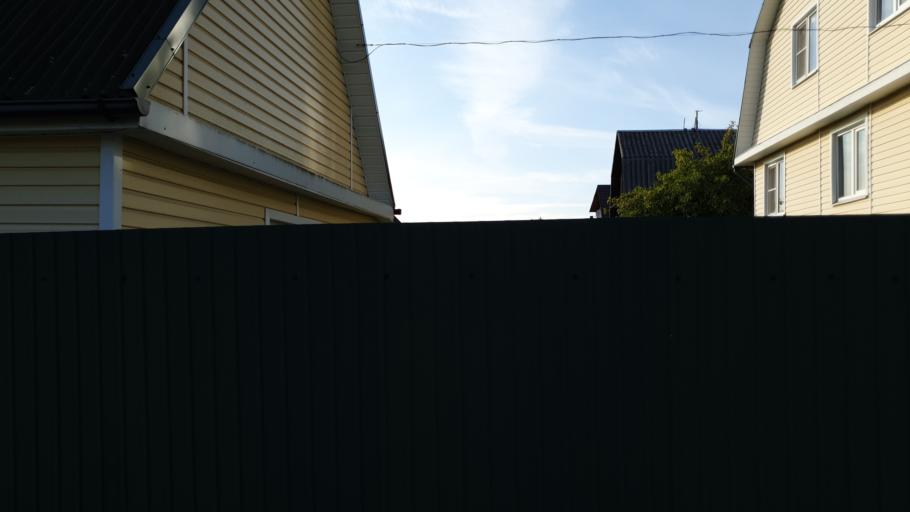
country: RU
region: Leningrad
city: Ivangorod
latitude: 59.4256
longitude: 28.3285
